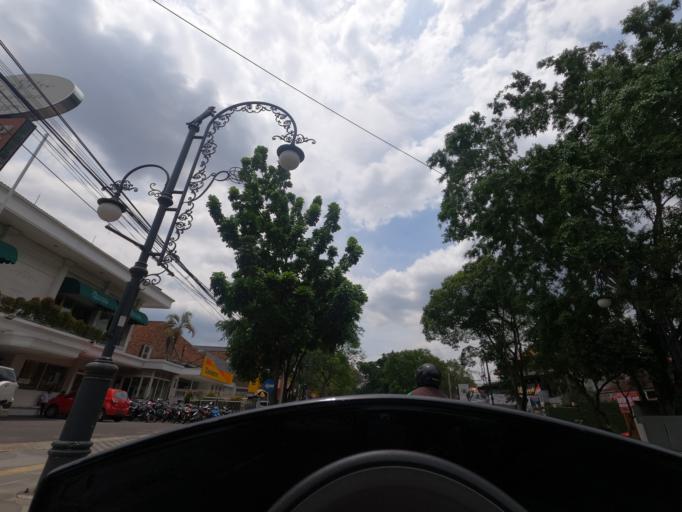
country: ID
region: West Java
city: Bandung
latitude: -6.9121
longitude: 107.6281
